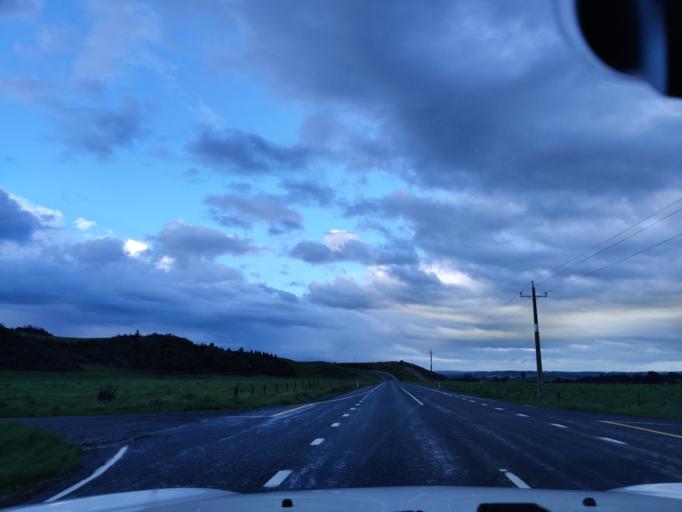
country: NZ
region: Waikato
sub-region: South Waikato District
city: Tokoroa
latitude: -38.3819
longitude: 175.7855
